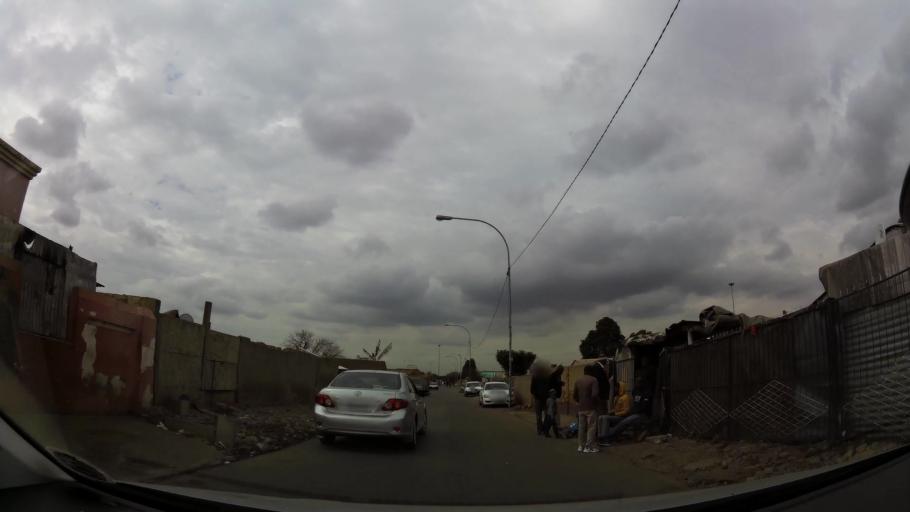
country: ZA
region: Gauteng
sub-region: City of Johannesburg Metropolitan Municipality
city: Soweto
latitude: -26.2784
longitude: 27.8601
